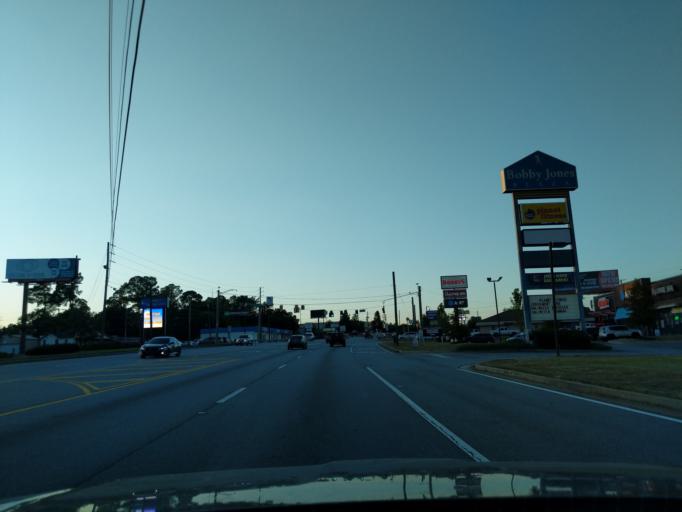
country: US
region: Georgia
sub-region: Columbia County
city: Martinez
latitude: 33.5076
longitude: -82.0928
